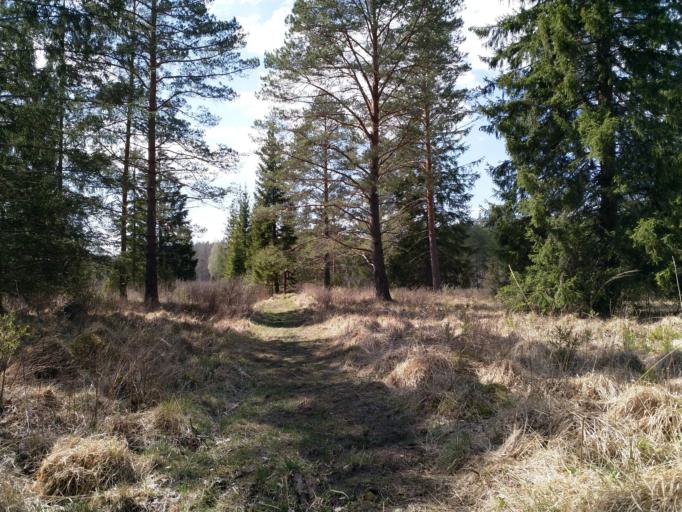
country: LV
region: Kandava
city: Kandava
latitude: 57.0176
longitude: 22.7742
